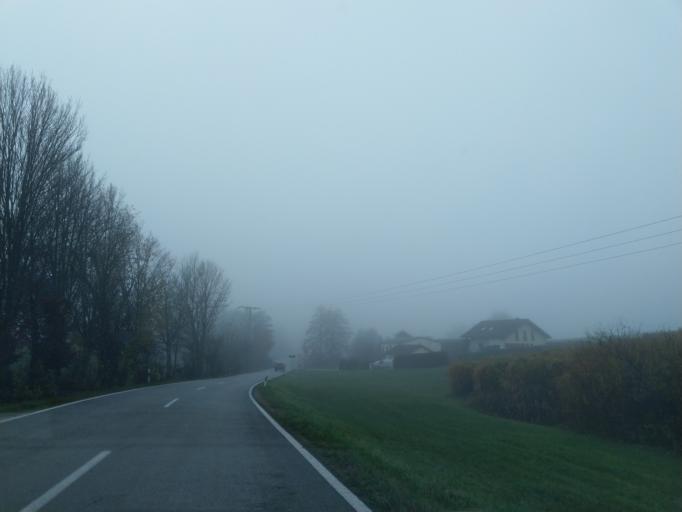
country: DE
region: Bavaria
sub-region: Lower Bavaria
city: Auerbach
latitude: 48.7748
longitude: 13.0952
